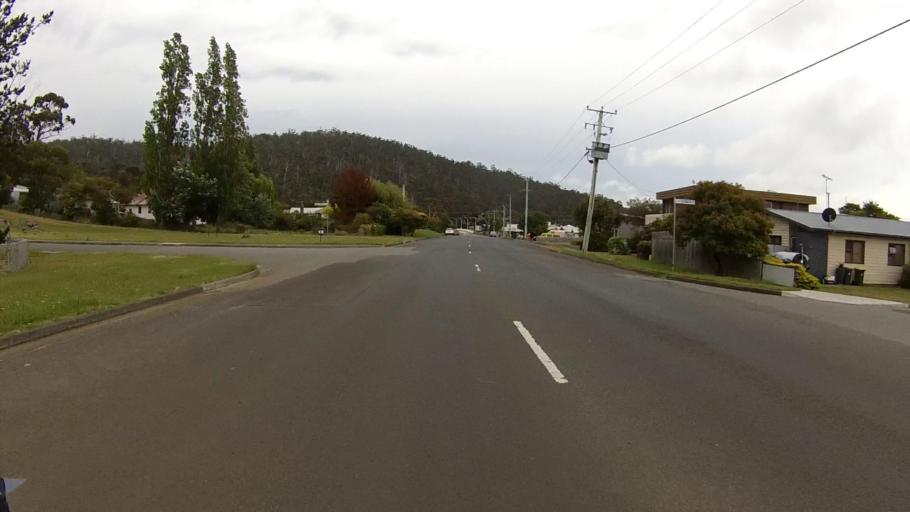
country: AU
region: Tasmania
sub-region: Sorell
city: Sorell
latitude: -42.5608
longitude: 147.8722
